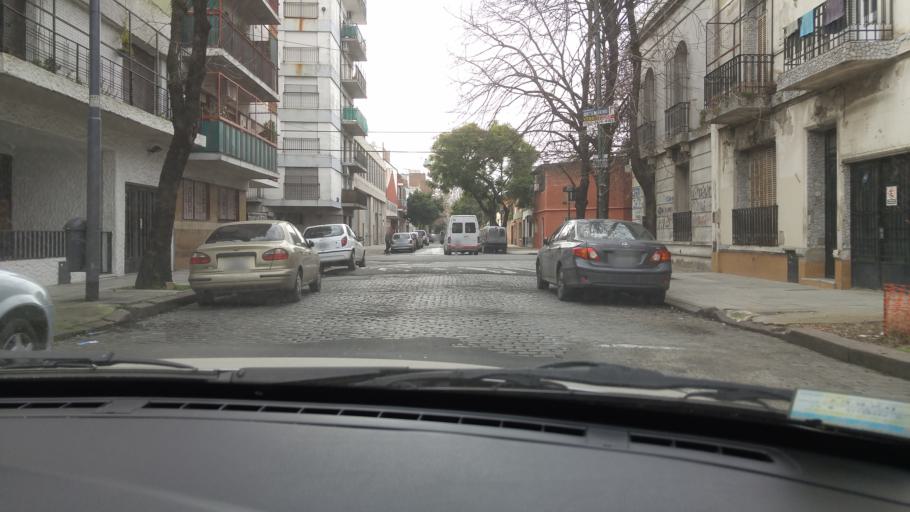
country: AR
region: Buenos Aires F.D.
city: Villa Santa Rita
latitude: -34.6277
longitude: -58.4864
